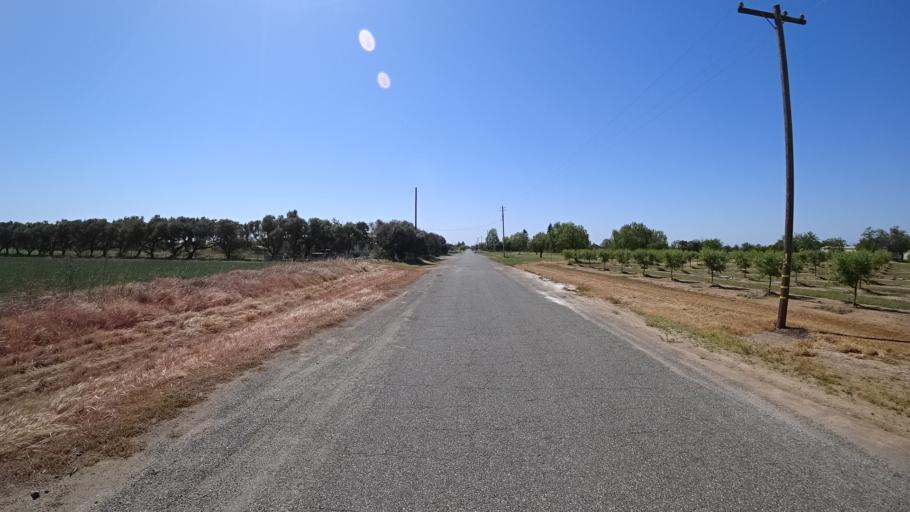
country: US
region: California
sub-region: Glenn County
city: Orland
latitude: 39.7837
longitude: -122.1597
